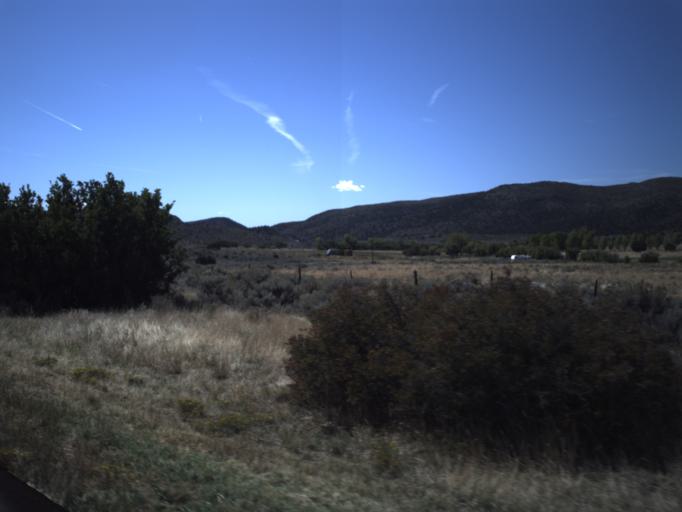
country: US
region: Utah
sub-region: Washington County
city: Enterprise
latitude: 37.4935
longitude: -113.6306
